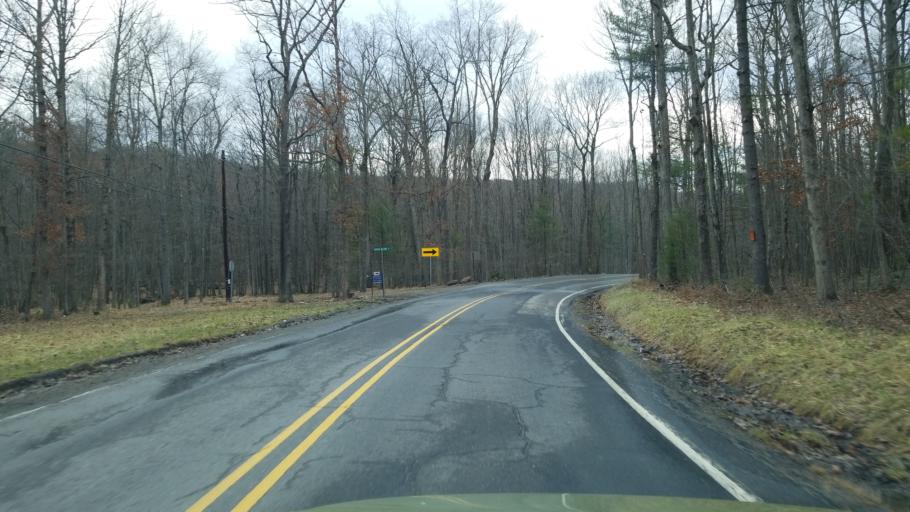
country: US
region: Pennsylvania
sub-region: Clearfield County
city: Clearfield
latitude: 41.0524
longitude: -78.4891
